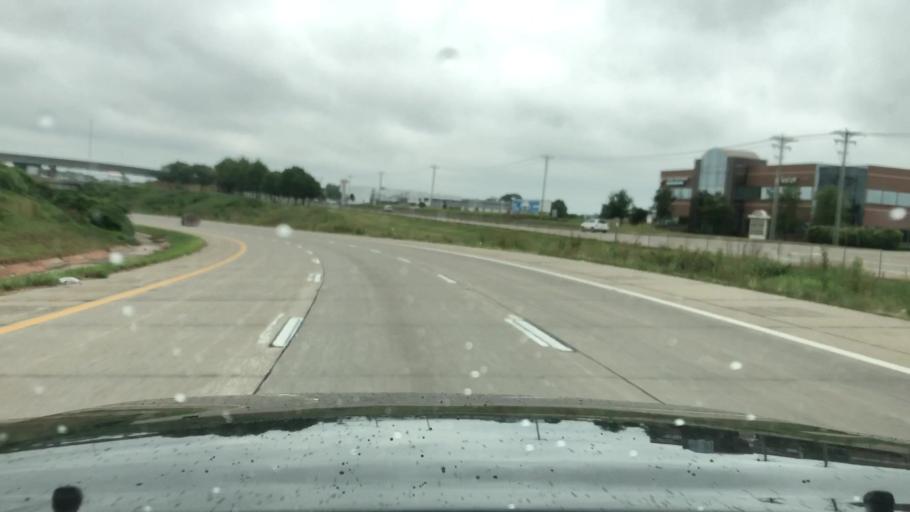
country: US
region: Missouri
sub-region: Saint Charles County
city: Saint Peters
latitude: 38.7979
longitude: -90.5950
